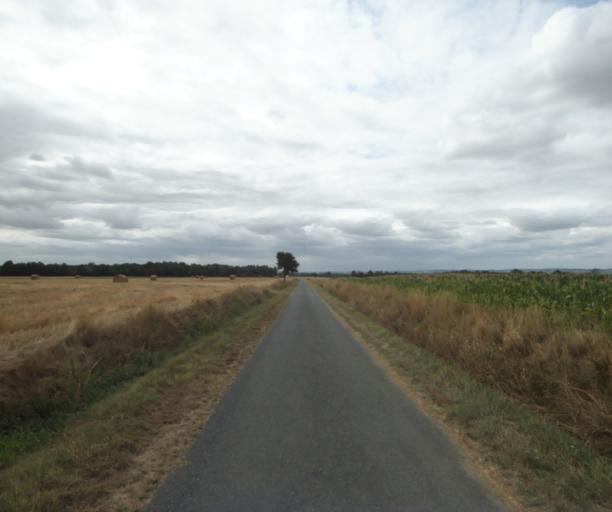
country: FR
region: Midi-Pyrenees
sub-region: Departement du Tarn
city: Soreze
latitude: 43.4662
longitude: 2.0488
